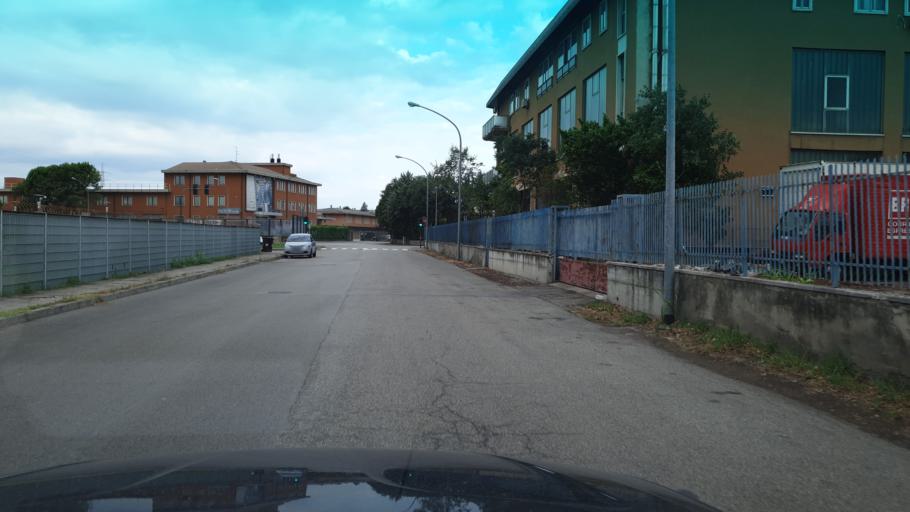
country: IT
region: Veneto
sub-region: Provincia di Verona
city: Verona
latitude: 45.3997
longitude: 10.9822
